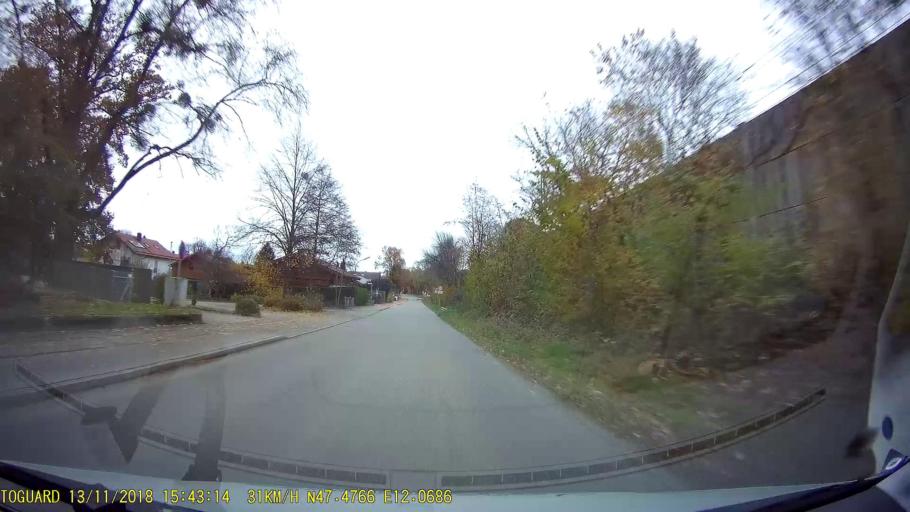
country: DE
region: Bavaria
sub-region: Upper Bavaria
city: Raubling
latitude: 47.7978
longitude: 12.1165
